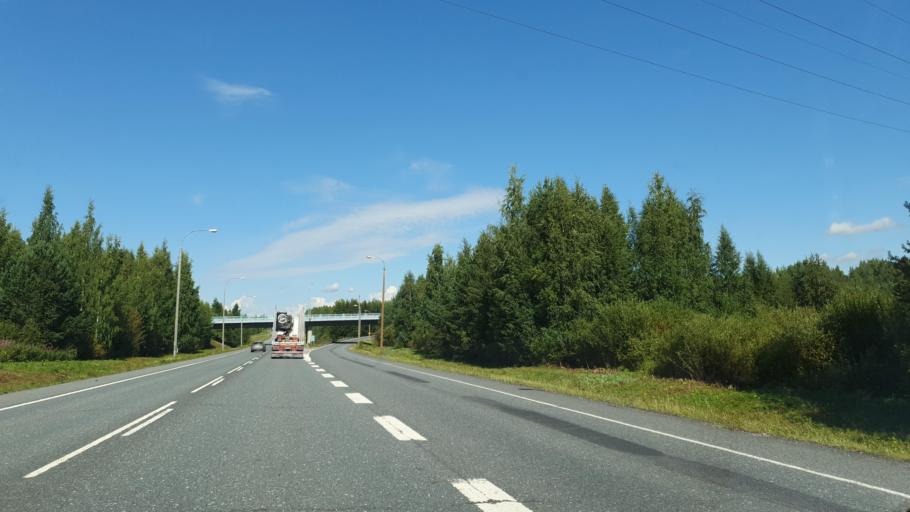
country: FI
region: Northern Savo
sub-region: Ylae-Savo
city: Iisalmi
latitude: 63.5891
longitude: 27.2261
